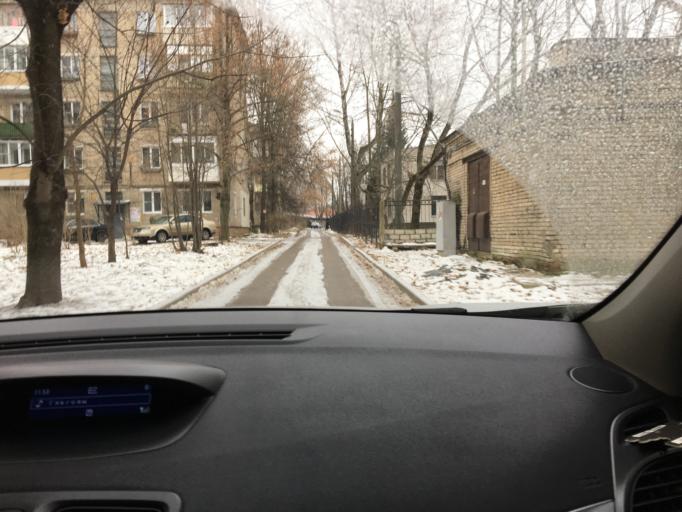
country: RU
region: Tula
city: Mendeleyevskiy
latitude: 54.1637
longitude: 37.5780
